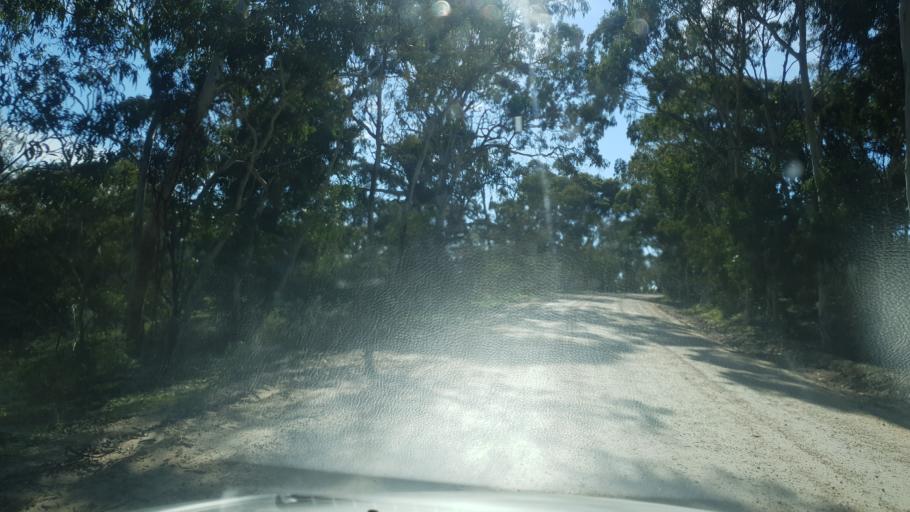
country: AU
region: South Australia
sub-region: Barossa
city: Williamstown
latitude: -34.6427
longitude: 138.8363
